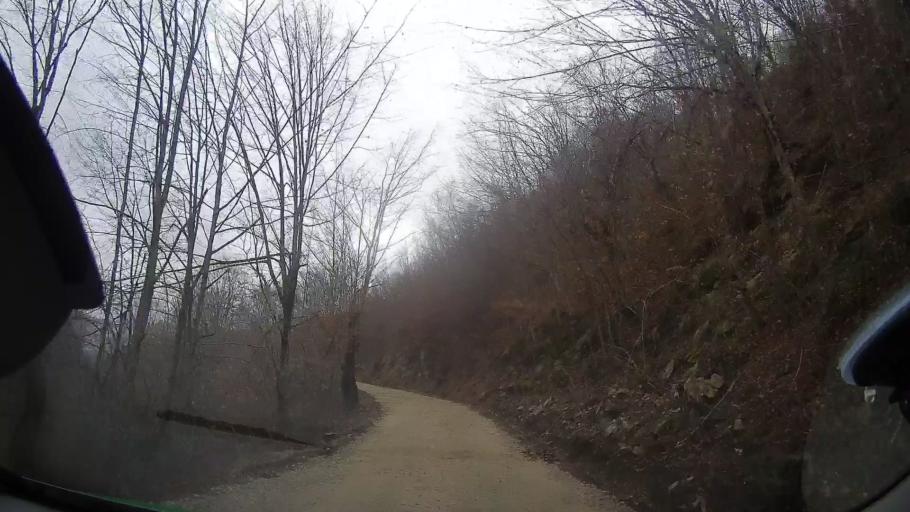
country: RO
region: Cluj
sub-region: Comuna Maguri-Racatau
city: Maguri-Racatau
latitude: 46.6522
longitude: 23.1928
